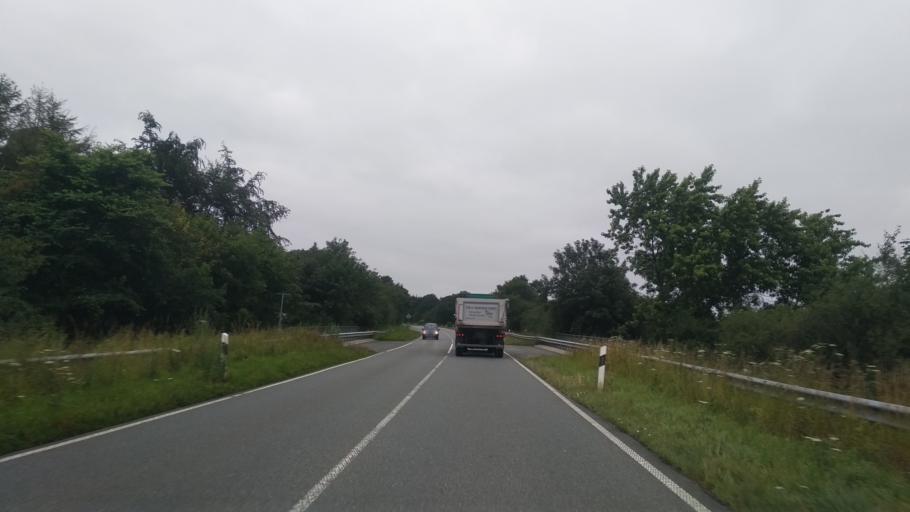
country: DE
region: Schleswig-Holstein
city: Sieverstedt
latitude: 54.6396
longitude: 9.4651
